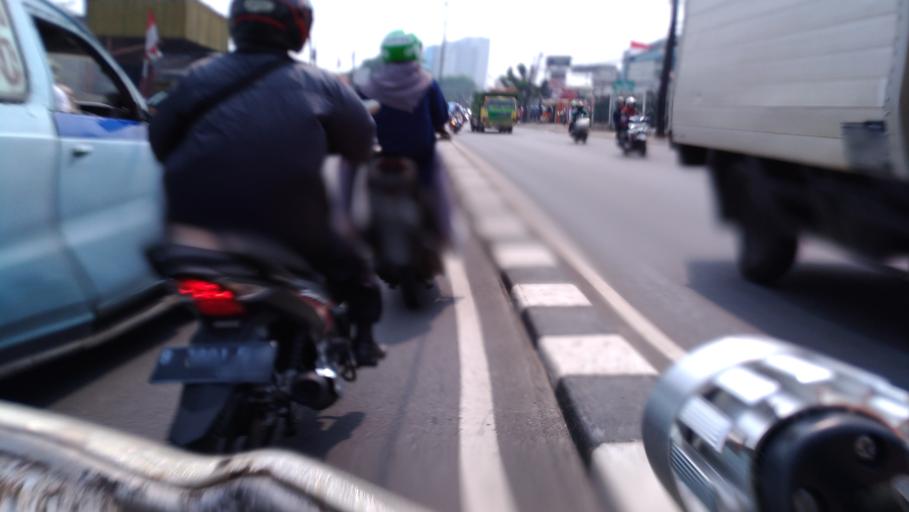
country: ID
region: West Java
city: Depok
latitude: -6.3458
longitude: 106.8677
